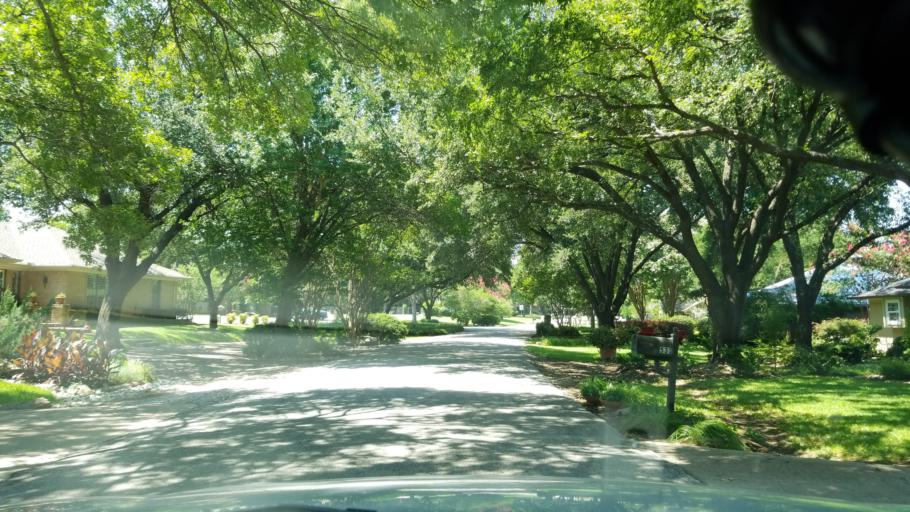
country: US
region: Texas
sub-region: Dallas County
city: Coppell
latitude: 32.9573
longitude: -96.9863
